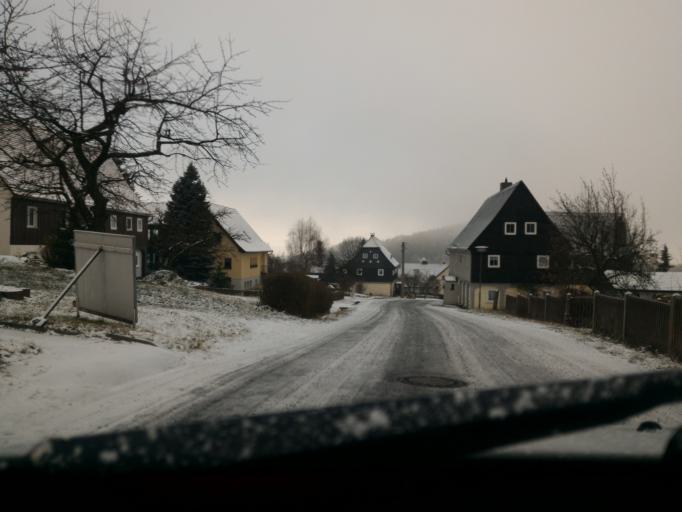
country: DE
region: Saxony
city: Grossschonau
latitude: 50.8556
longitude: 14.6543
